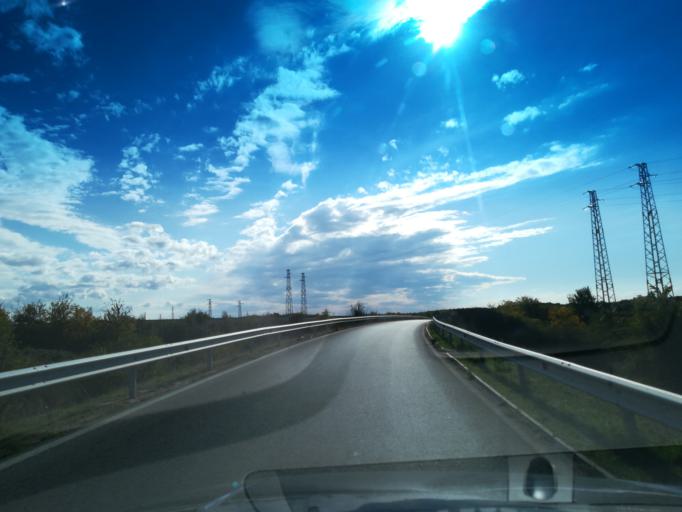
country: BG
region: Stara Zagora
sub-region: Obshtina Stara Zagora
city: Stara Zagora
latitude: 42.3415
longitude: 25.6608
